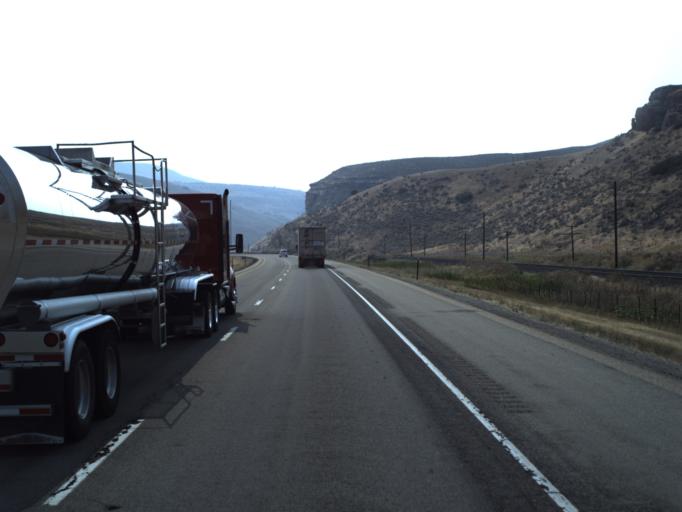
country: US
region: Utah
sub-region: Summit County
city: Coalville
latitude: 41.0386
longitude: -111.3284
